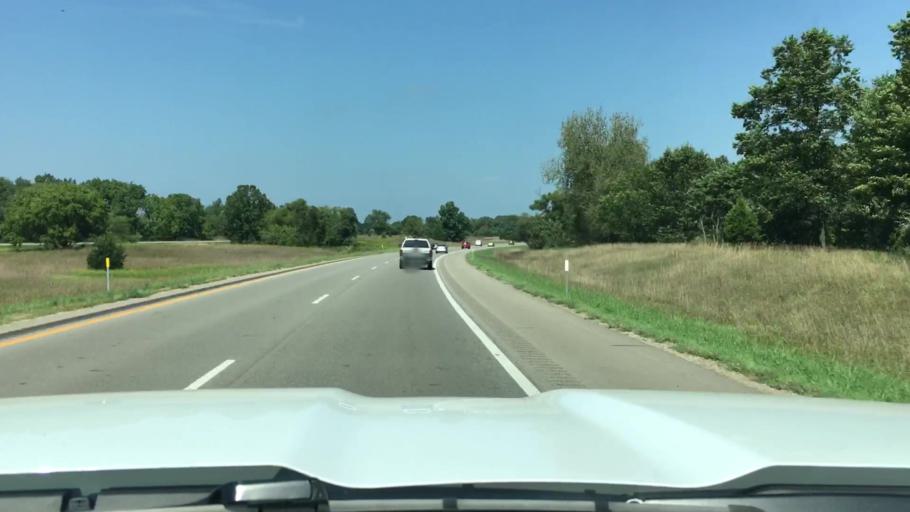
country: US
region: Michigan
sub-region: Kalamazoo County
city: Schoolcraft
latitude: 42.1542
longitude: -85.6425
